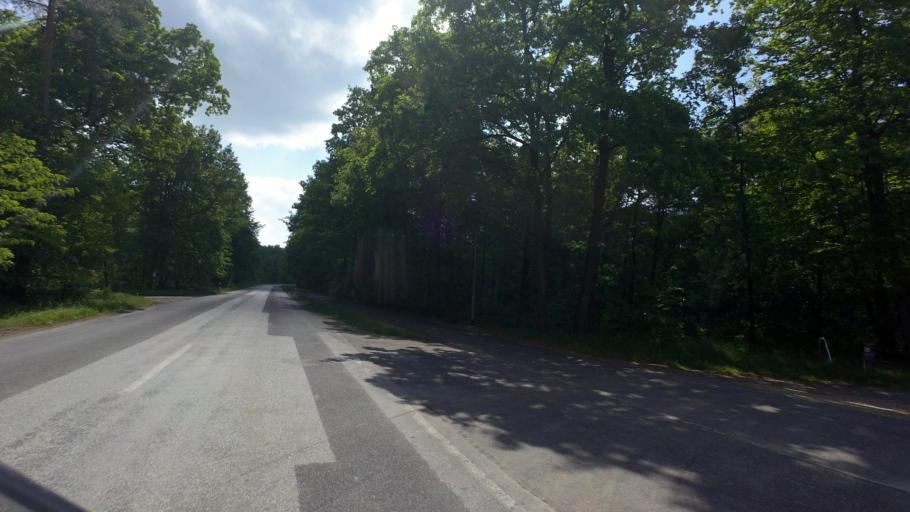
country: DE
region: Saxony
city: Mucka
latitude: 51.3077
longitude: 14.6808
